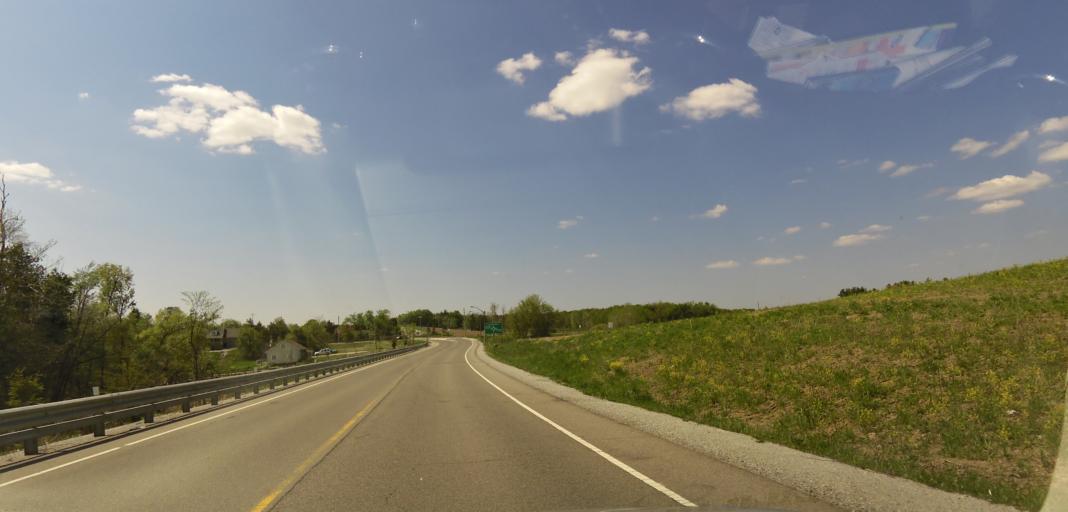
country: CA
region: Ontario
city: Brampton
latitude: 43.8283
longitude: -79.8814
